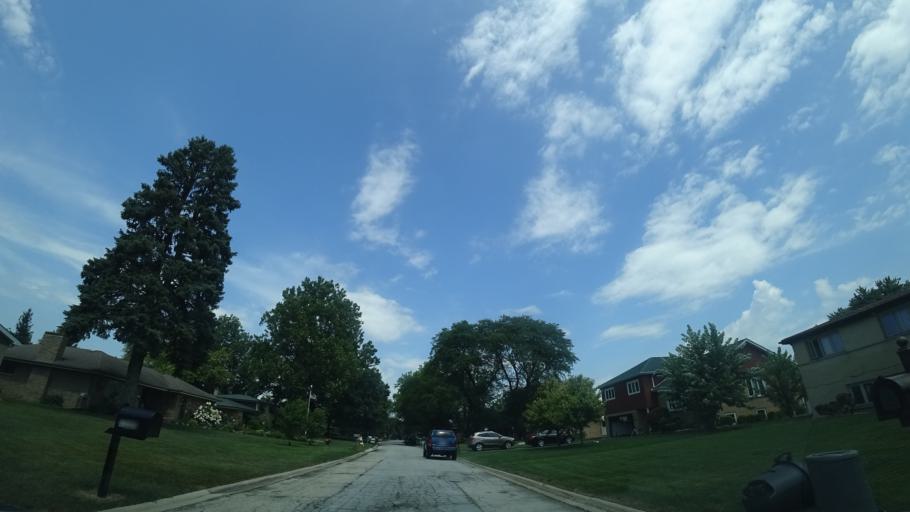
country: US
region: Illinois
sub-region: Cook County
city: Crestwood
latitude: 41.6623
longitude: -87.7694
